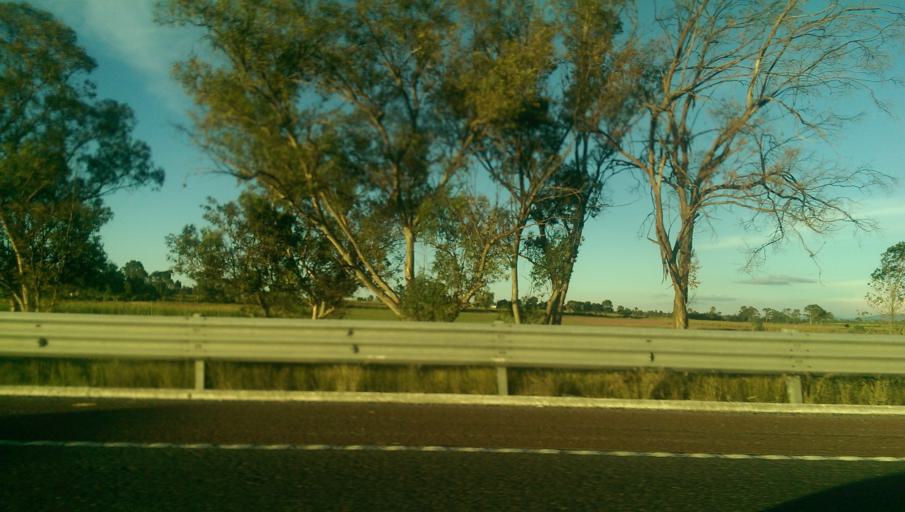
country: MX
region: Queretaro
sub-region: San Juan del Rio
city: El Cazadero
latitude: 20.2600
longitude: -99.8524
